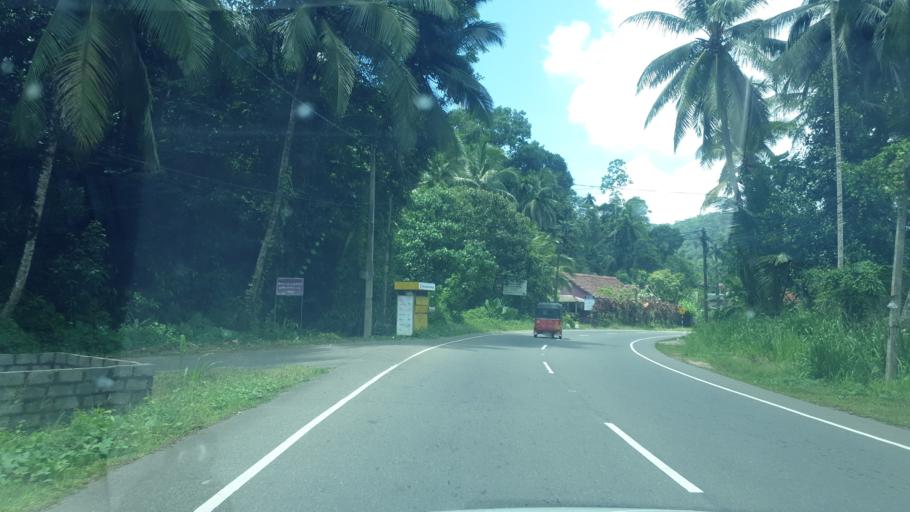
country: LK
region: Western
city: Horawala Junction
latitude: 6.5242
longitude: 80.1933
